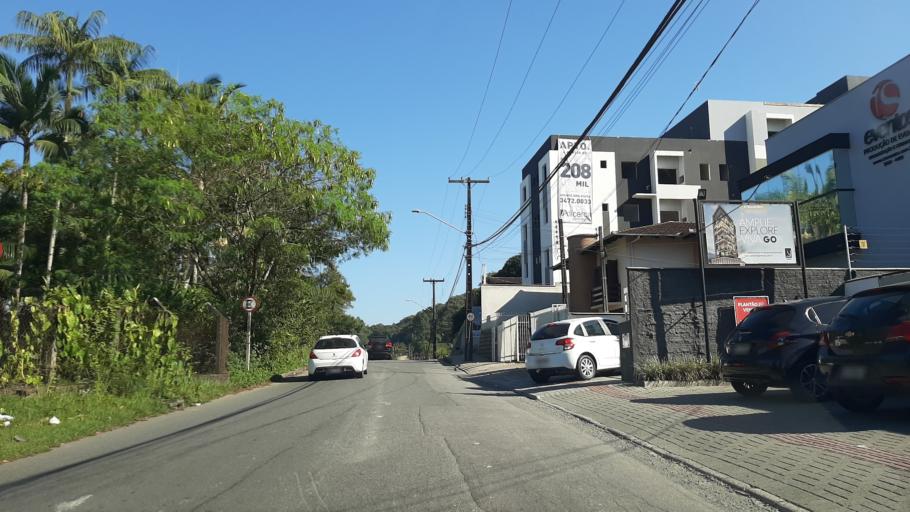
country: BR
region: Santa Catarina
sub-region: Joinville
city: Joinville
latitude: -26.3131
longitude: -48.8601
